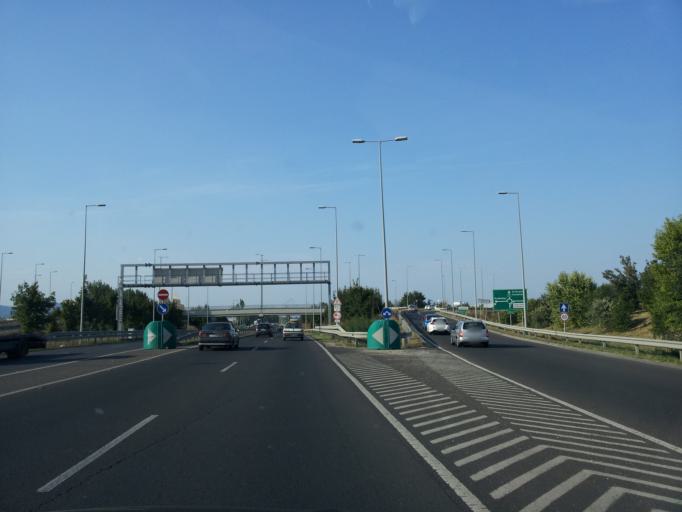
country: HU
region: Pest
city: Budakalasz
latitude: 47.6183
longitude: 19.0661
